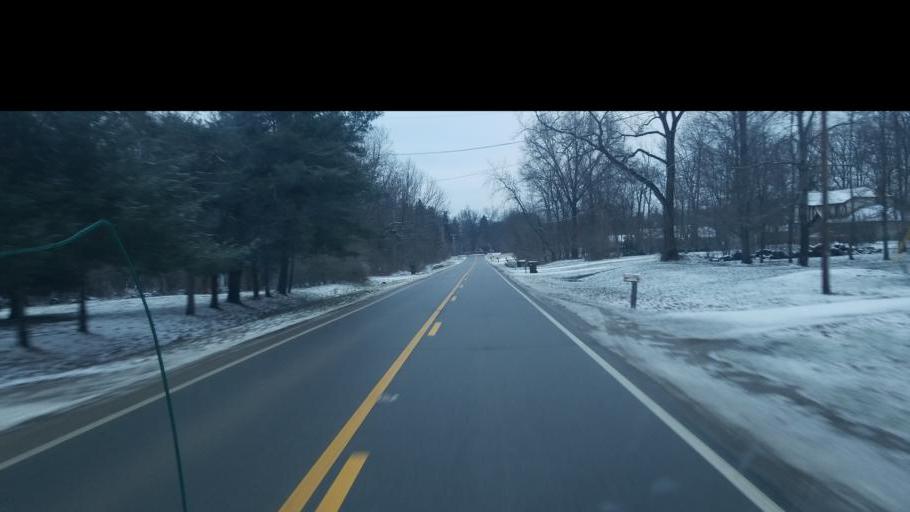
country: US
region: Ohio
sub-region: Franklin County
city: Huber Ridge
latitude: 40.1148
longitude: -82.8719
